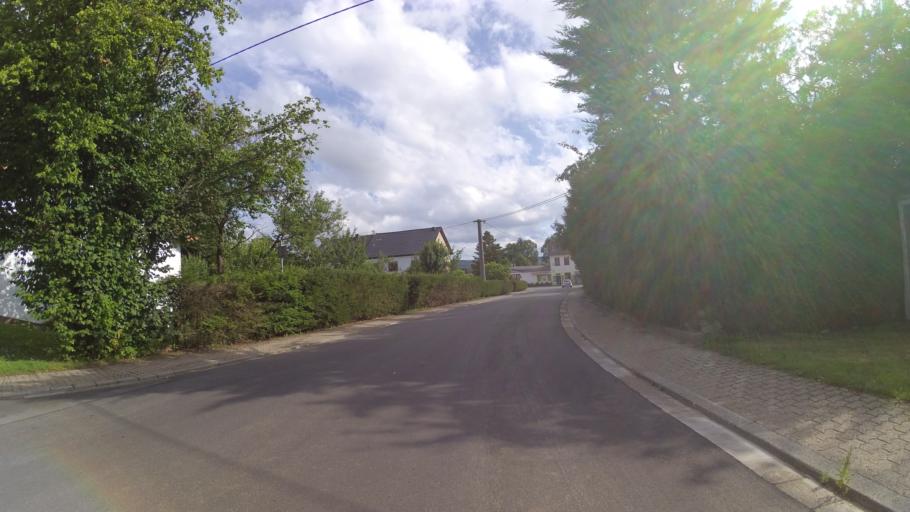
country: DE
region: Rheinland-Pfalz
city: Neuhutten
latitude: 49.6042
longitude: 6.9912
